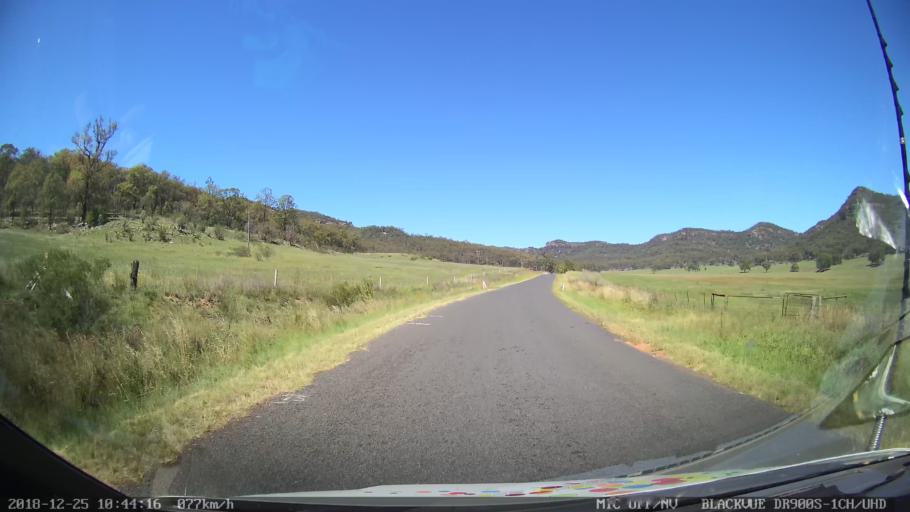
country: AU
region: New South Wales
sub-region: Upper Hunter Shire
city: Merriwa
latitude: -32.4275
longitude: 150.3029
